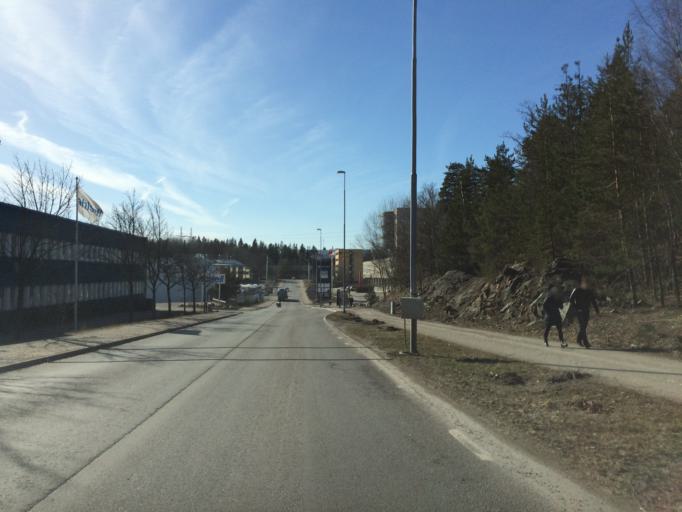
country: SE
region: Stockholm
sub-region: Huddinge Kommun
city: Segeltorp
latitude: 59.2652
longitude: 17.9069
